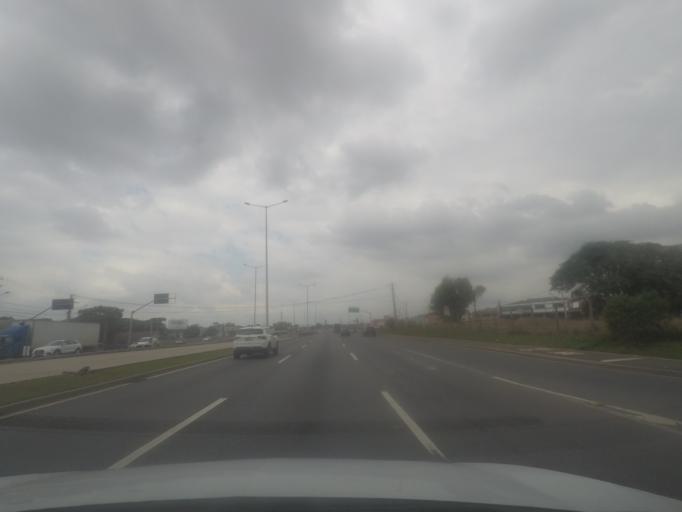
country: BR
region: Parana
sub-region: Sao Jose Dos Pinhais
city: Sao Jose dos Pinhais
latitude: -25.5213
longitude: -49.2945
